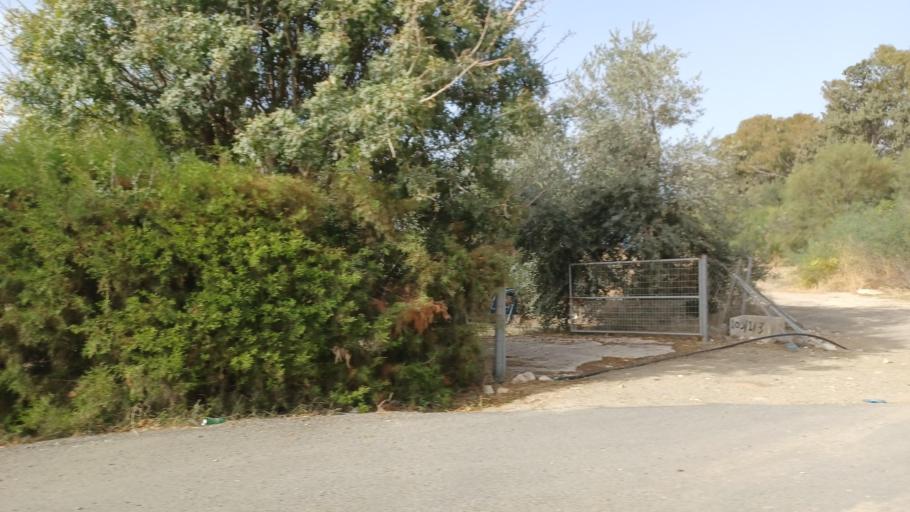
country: CY
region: Pafos
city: Polis
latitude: 35.0410
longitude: 32.4174
